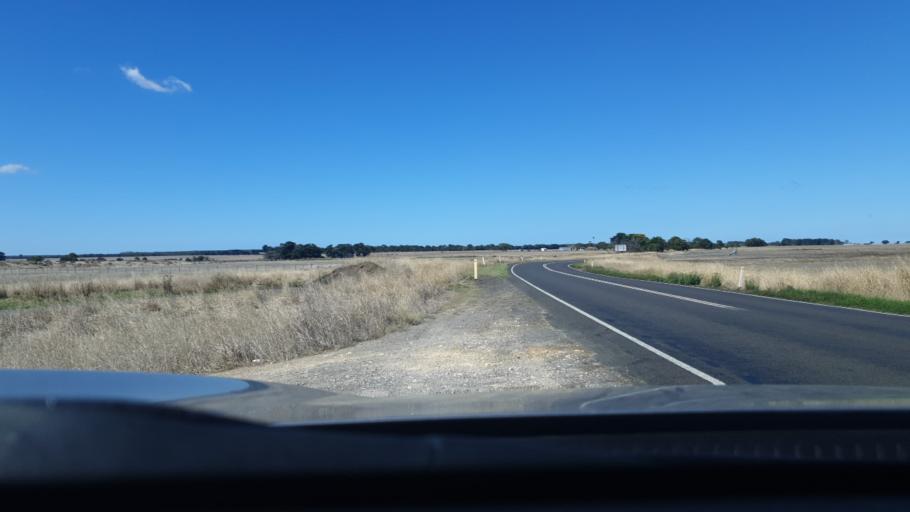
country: AU
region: Victoria
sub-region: Glenelg
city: Portland
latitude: -38.1531
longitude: 141.7717
